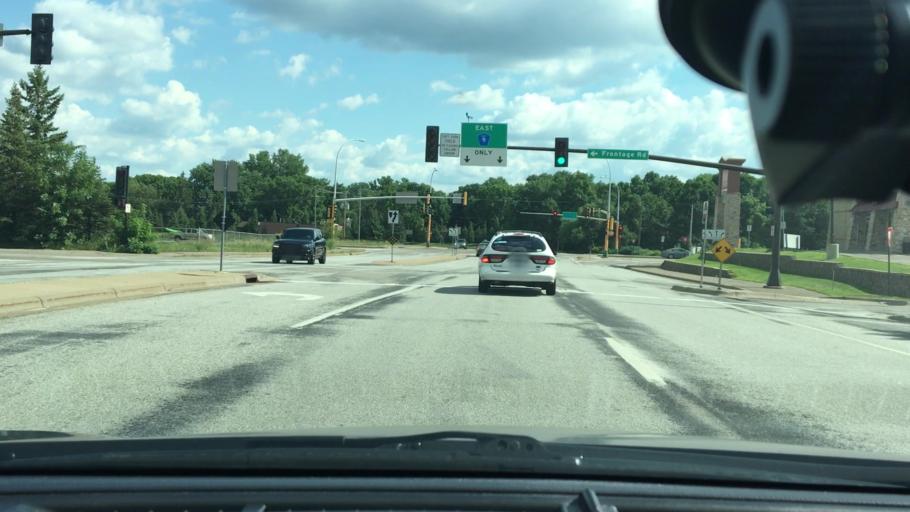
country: US
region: Minnesota
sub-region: Hennepin County
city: New Hope
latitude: 45.0343
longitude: -93.4084
